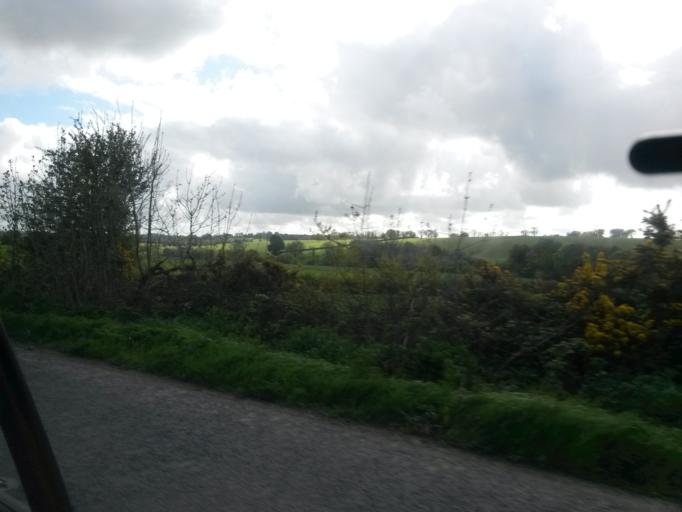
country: IE
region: Leinster
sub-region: Loch Garman
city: Ferns
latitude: 52.5694
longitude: -6.5226
